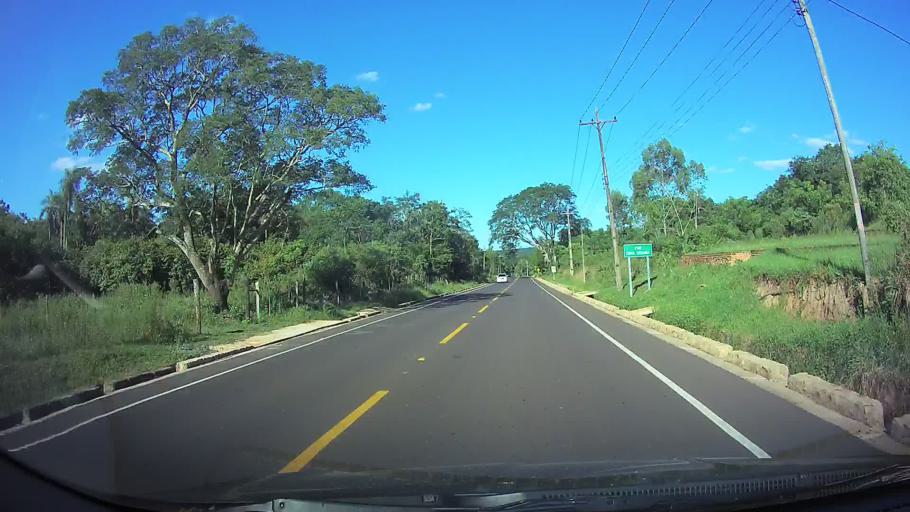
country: PY
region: Cordillera
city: Caacupe
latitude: -25.3238
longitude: -57.1540
